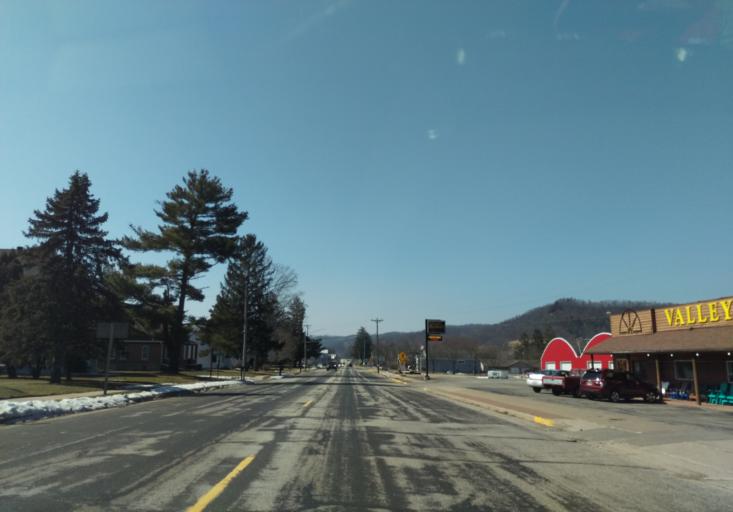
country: US
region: Wisconsin
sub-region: Vernon County
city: Westby
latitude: 43.7024
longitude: -91.0101
